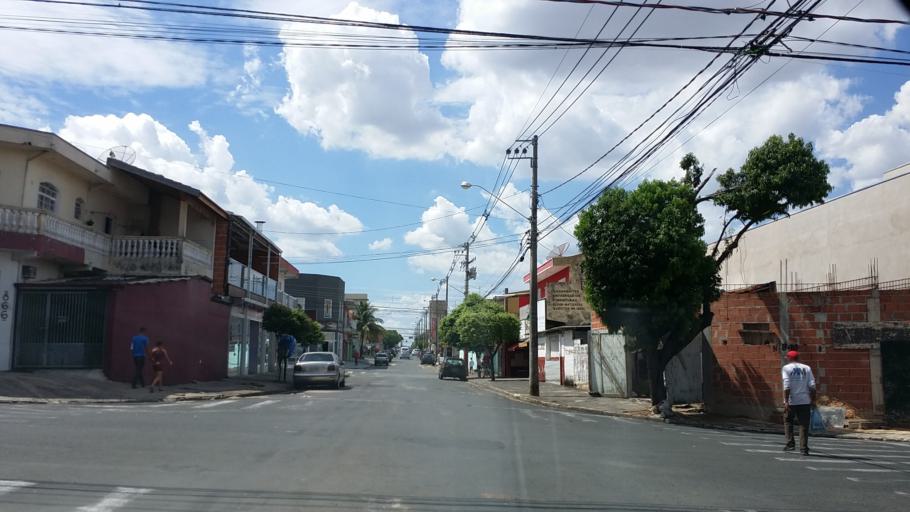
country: BR
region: Sao Paulo
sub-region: Indaiatuba
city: Indaiatuba
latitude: -23.1204
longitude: -47.2421
